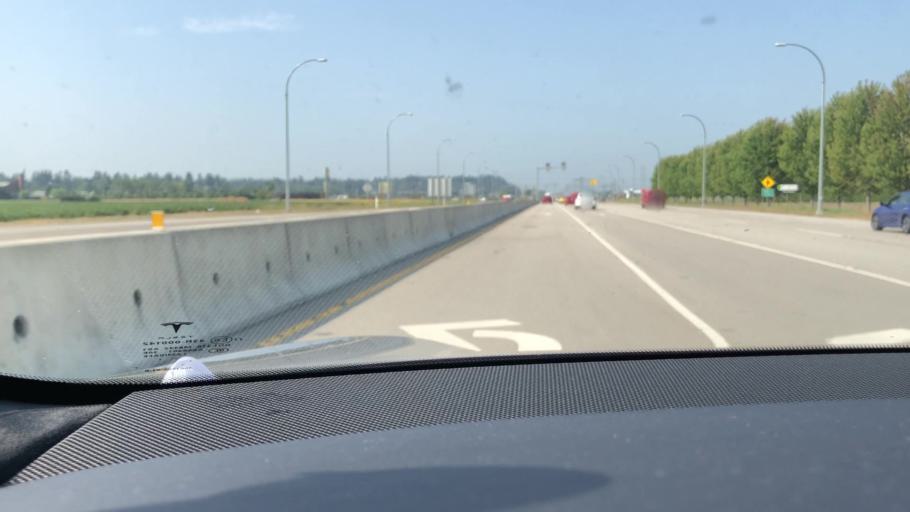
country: CA
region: British Columbia
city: Ladner
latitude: 49.0451
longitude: -123.0640
